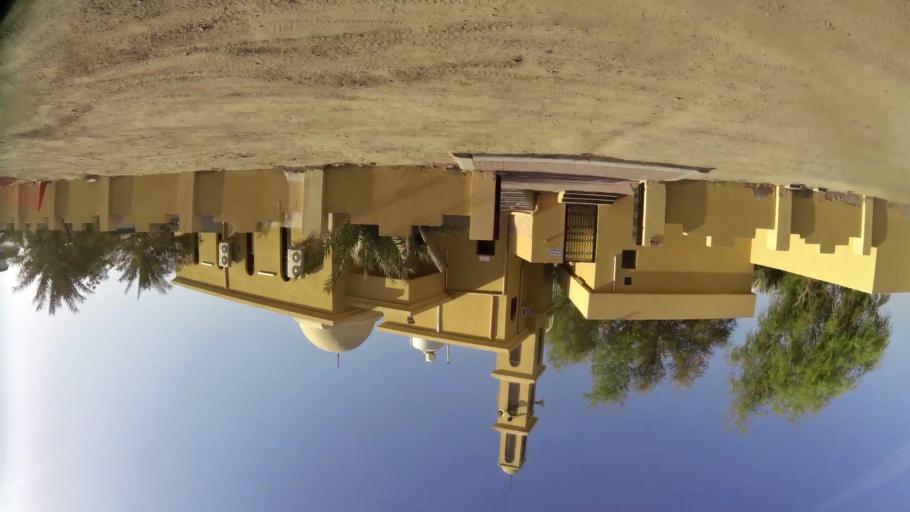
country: AE
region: Ajman
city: Ajman
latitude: 25.4079
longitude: 55.4638
